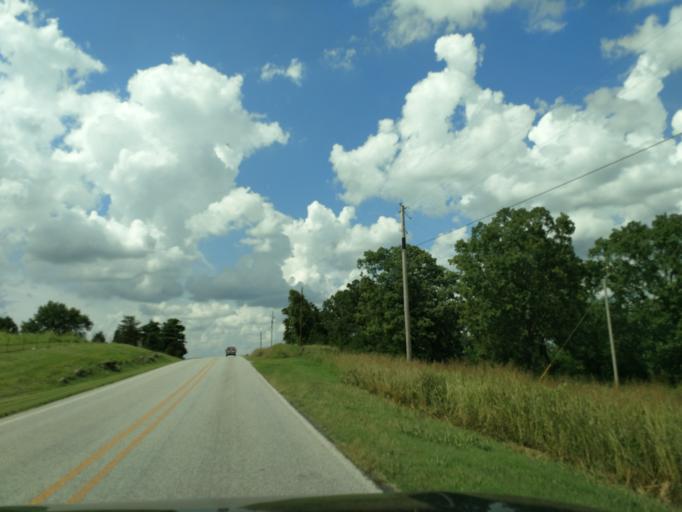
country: US
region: Arkansas
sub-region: Carroll County
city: Berryville
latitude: 36.4474
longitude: -93.5561
